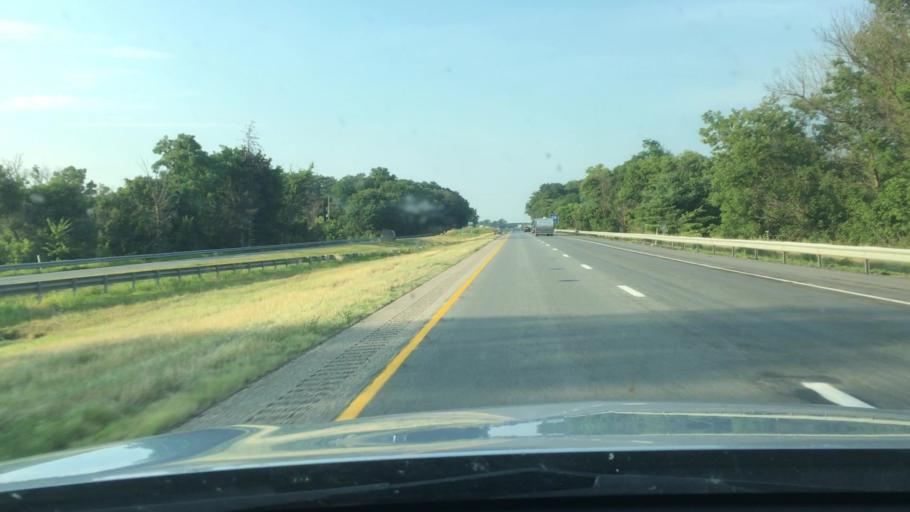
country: US
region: Pennsylvania
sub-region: Cumberland County
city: Shippensburg
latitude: 40.0502
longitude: -77.4866
